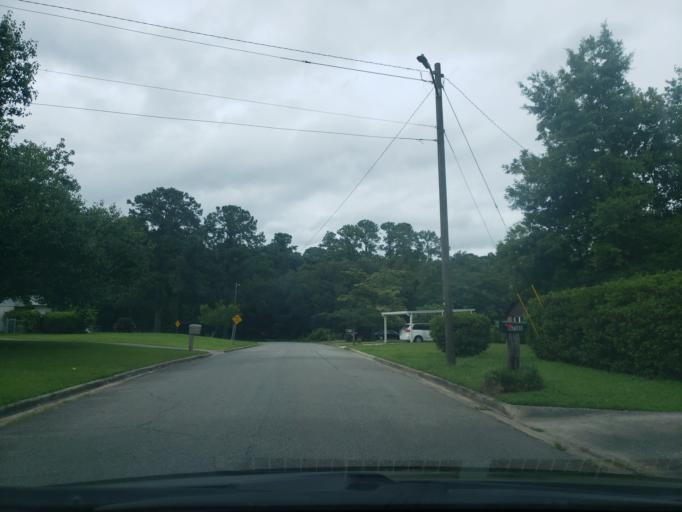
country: US
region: Georgia
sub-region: Chatham County
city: Montgomery
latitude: 31.9929
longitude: -81.1136
